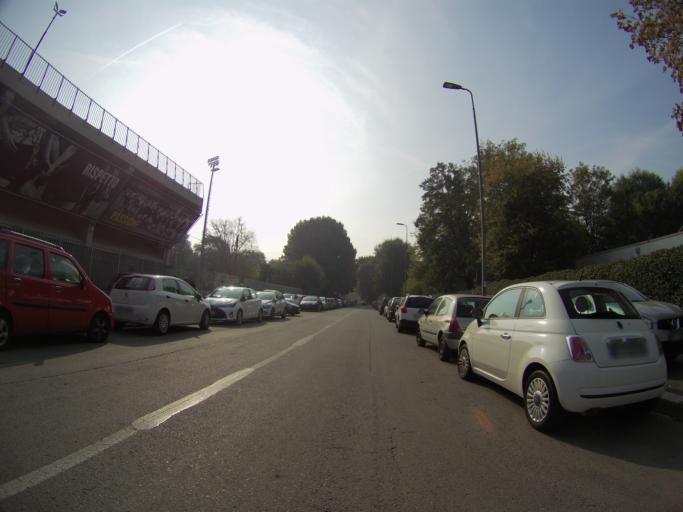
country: IT
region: Lombardy
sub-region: Citta metropolitana di Milano
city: Novegro-Tregarezzo-San Felice
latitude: 45.4760
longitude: 9.2366
